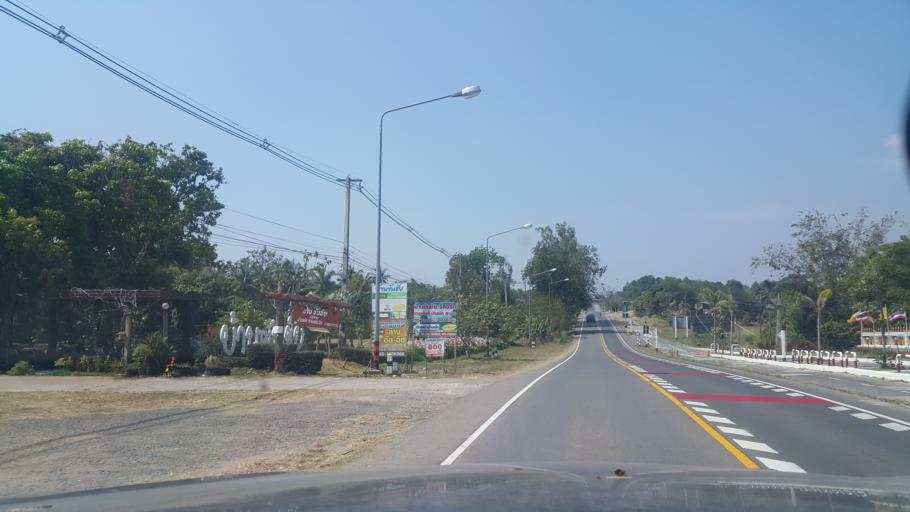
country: TH
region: Nakhon Ratchasima
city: Wang Nam Khiao
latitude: 14.3615
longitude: 101.9160
